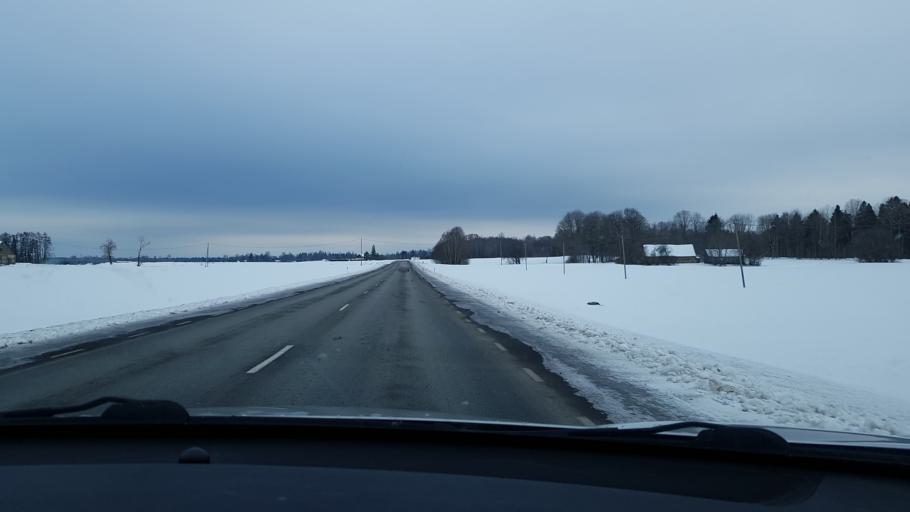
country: EE
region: Jaervamaa
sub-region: Paide linn
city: Paide
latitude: 58.8859
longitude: 25.7094
